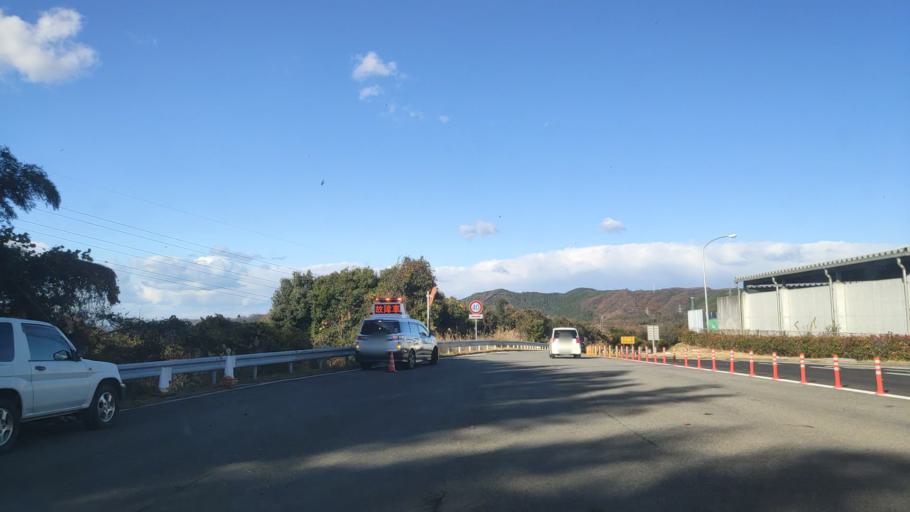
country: JP
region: Ehime
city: Saijo
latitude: 33.9147
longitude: 133.2368
